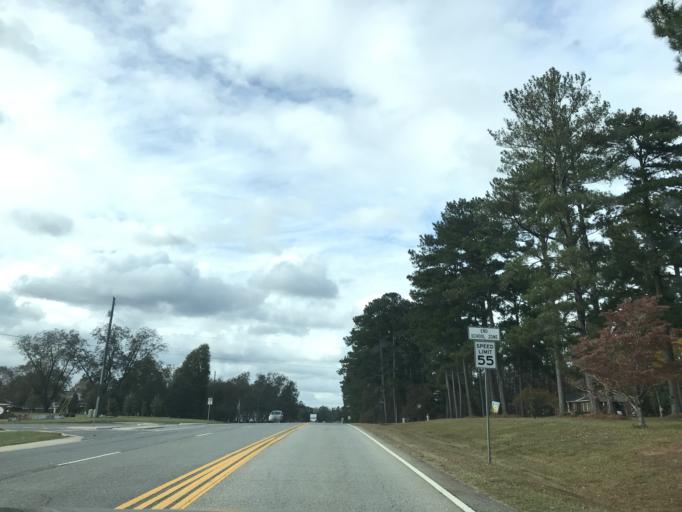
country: US
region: Georgia
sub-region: Jones County
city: Gray
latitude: 32.9967
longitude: -83.5265
